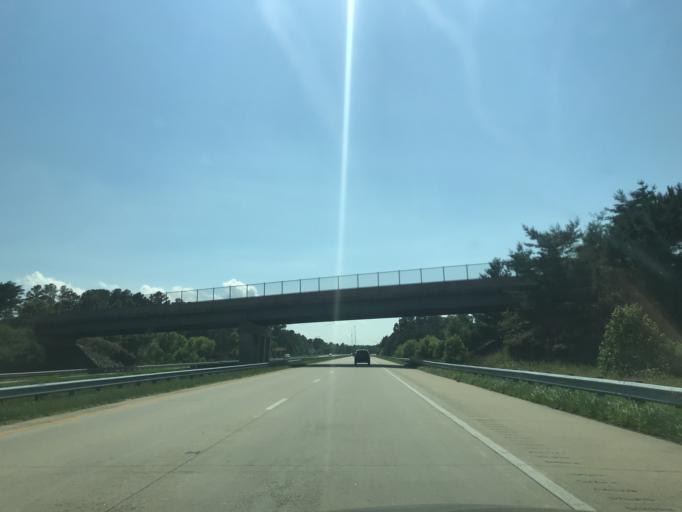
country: US
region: Maryland
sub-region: Wicomico County
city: Salisbury
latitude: 38.4022
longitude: -75.6192
